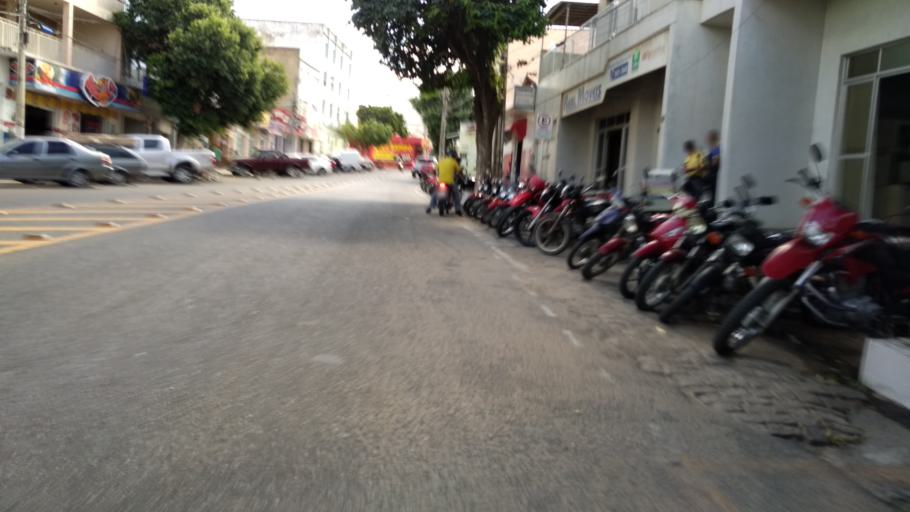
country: BR
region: Bahia
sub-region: Guanambi
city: Guanambi
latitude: -14.2292
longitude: -42.7803
